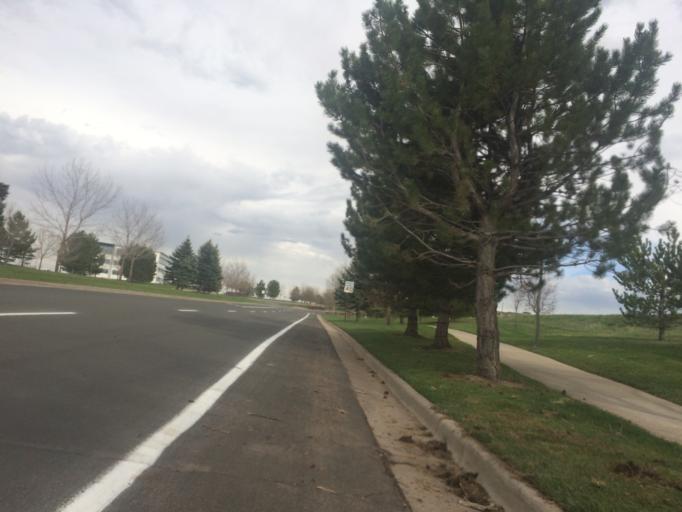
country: US
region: Colorado
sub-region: Broomfield County
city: Broomfield
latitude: 39.9196
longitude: -105.1080
